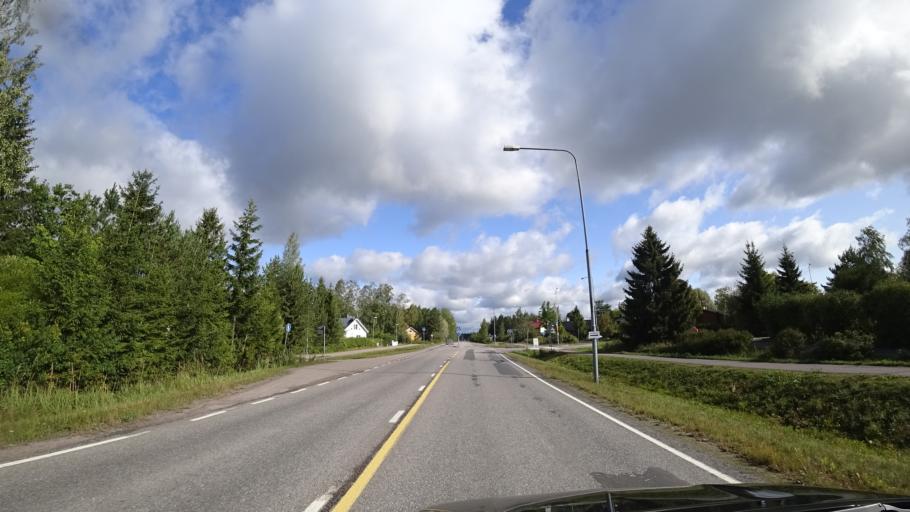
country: FI
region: Uusimaa
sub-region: Helsinki
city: Hyvinge
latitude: 60.5584
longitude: 24.9702
